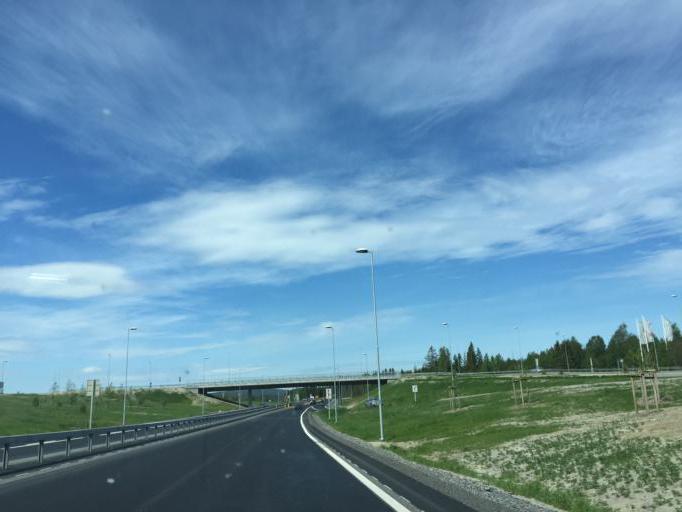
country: NO
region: Hedmark
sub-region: Sor-Odal
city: Skarnes
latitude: 60.2471
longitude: 11.7443
